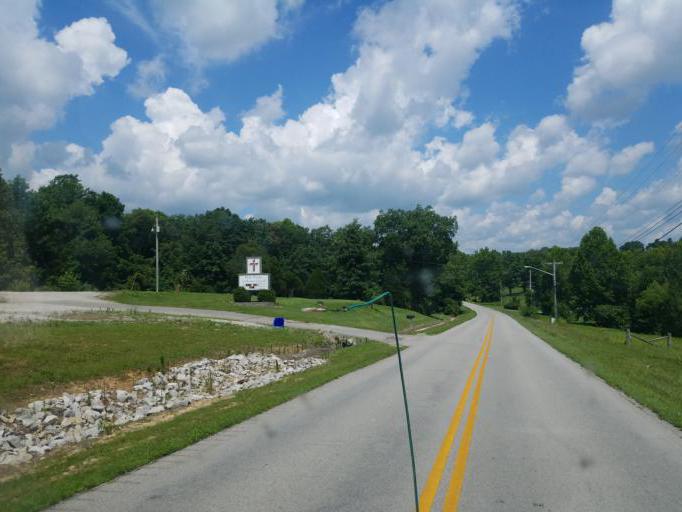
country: US
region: Kentucky
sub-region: Grayson County
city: Leitchfield
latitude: 37.4972
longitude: -86.3064
